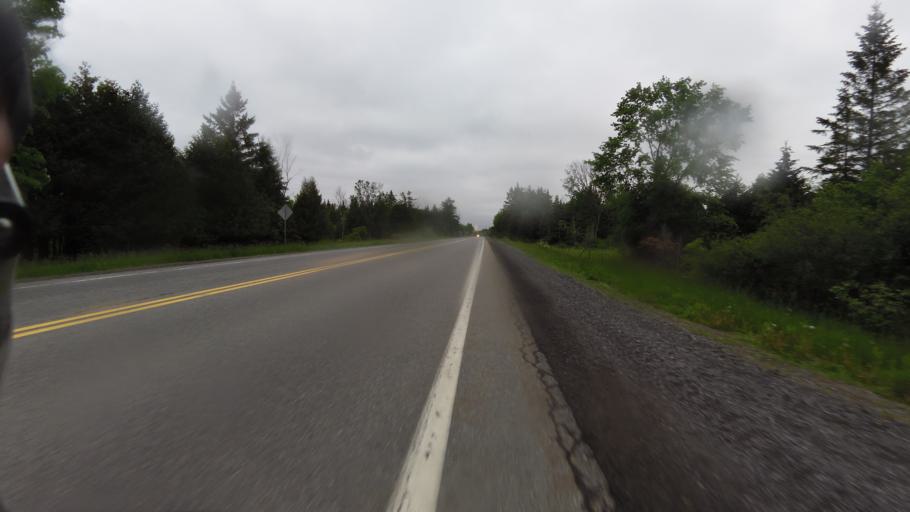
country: CA
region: Ontario
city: Bells Corners
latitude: 45.3154
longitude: -75.8663
